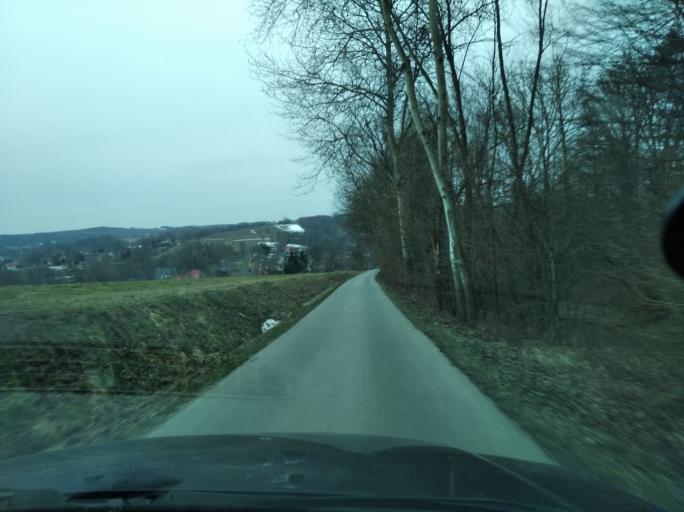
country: PL
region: Subcarpathian Voivodeship
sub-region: Powiat rzeszowski
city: Chmielnik
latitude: 49.9808
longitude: 22.1350
